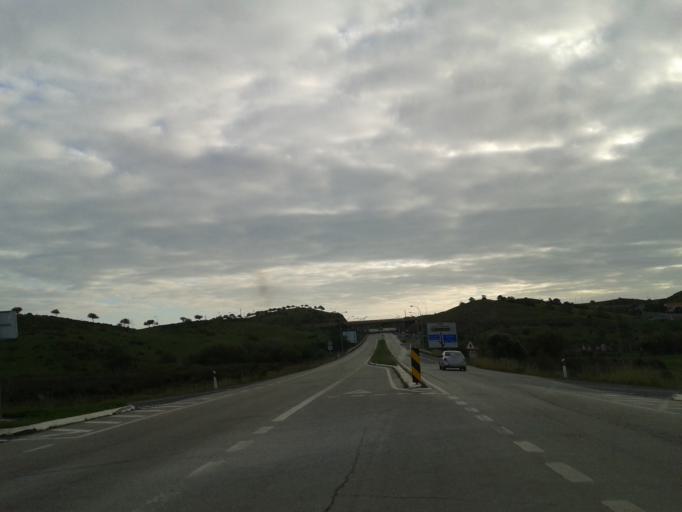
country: PT
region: Faro
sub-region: Castro Marim
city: Castro Marim
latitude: 37.2347
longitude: -7.4474
